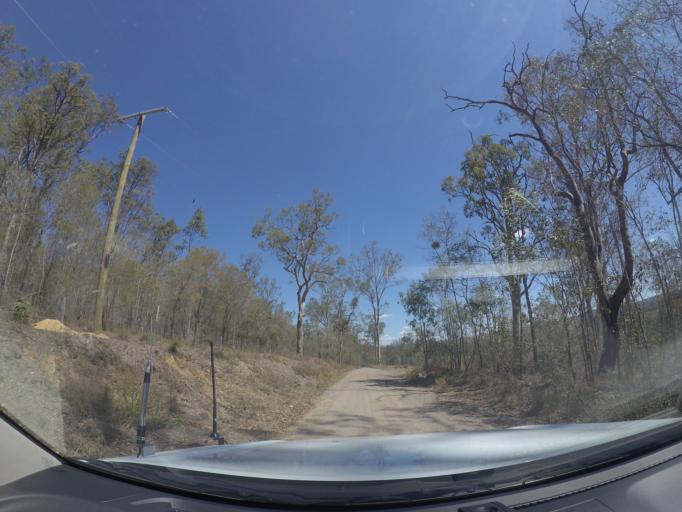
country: AU
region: Queensland
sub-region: Logan
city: North Maclean
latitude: -27.7732
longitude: 152.9375
